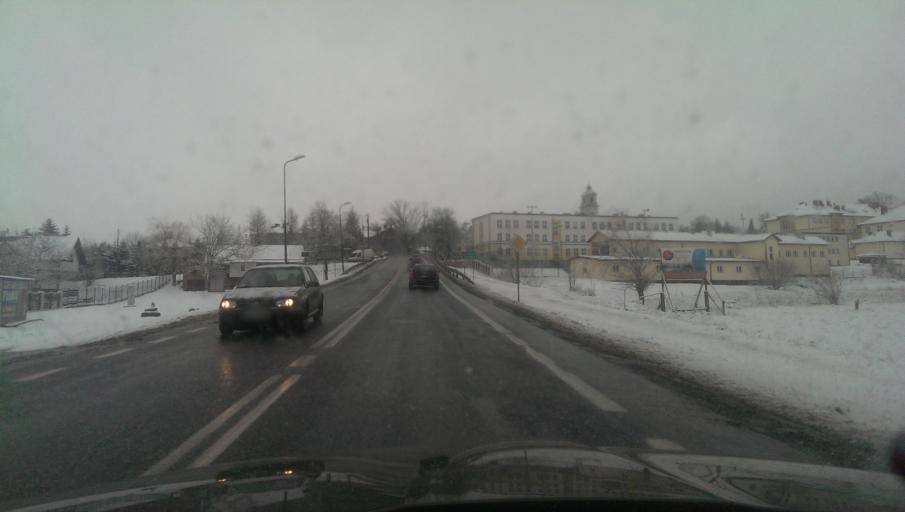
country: PL
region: Subcarpathian Voivodeship
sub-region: Powiat krosnienski
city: Rymanow
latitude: 49.5780
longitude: 21.8619
